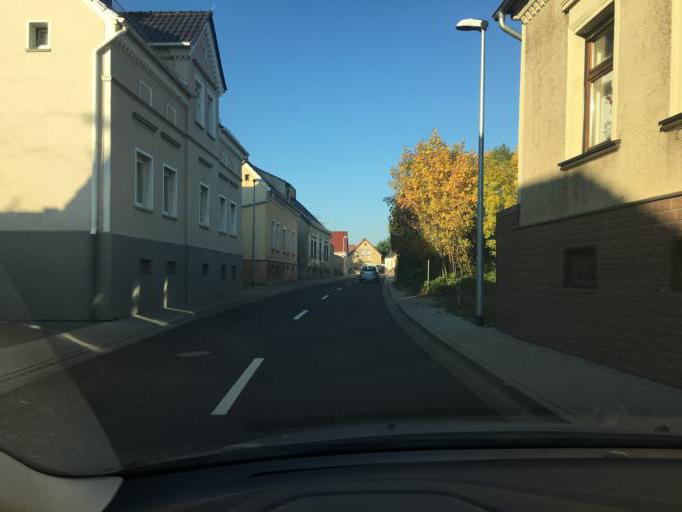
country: DE
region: Saxony-Anhalt
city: Borne
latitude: 52.0009
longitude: 11.5283
